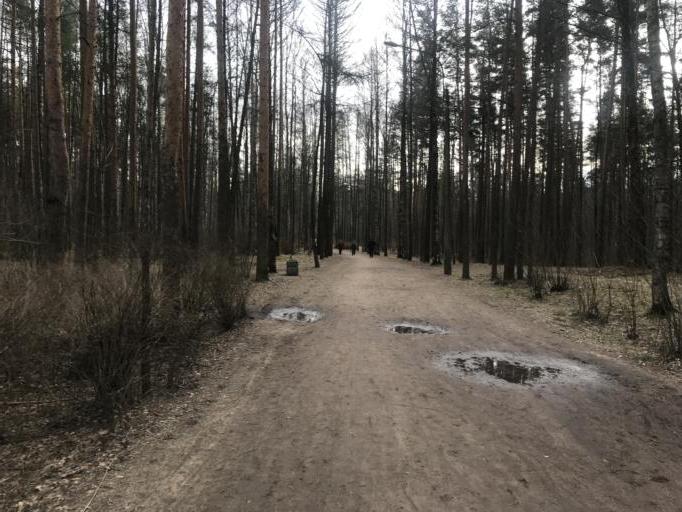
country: RU
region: St.-Petersburg
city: Sosnovka
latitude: 60.0185
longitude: 30.3455
